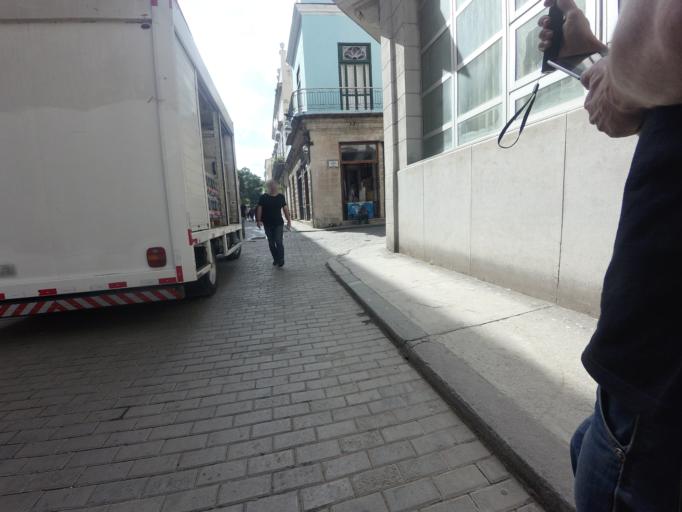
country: CU
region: La Habana
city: La Habana Vieja
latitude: 23.1367
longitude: -82.3487
